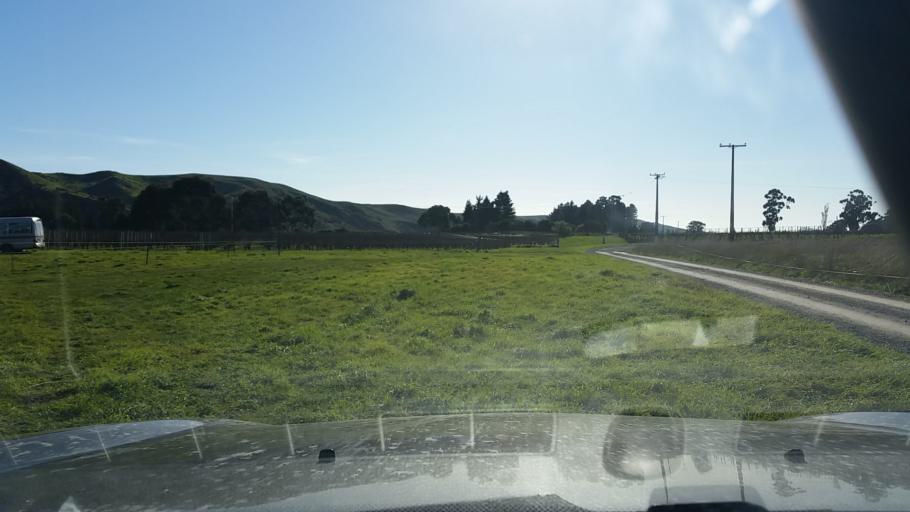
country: NZ
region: Marlborough
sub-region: Marlborough District
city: Blenheim
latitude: -41.6877
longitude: 174.1271
